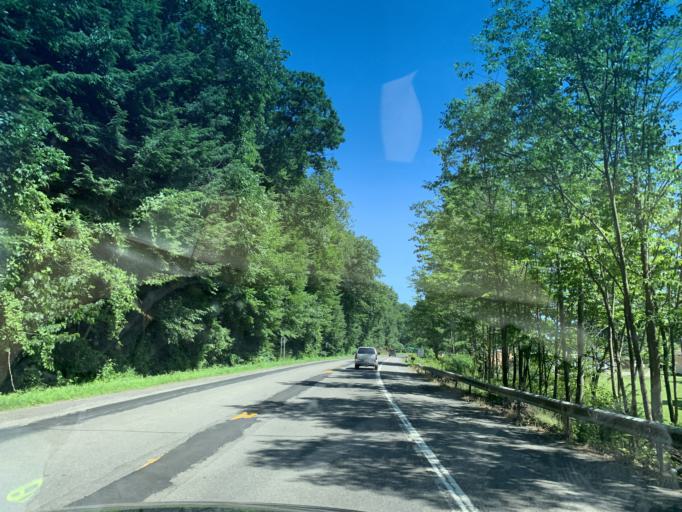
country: US
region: New York
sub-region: Delaware County
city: Sidney
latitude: 42.3823
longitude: -75.4079
